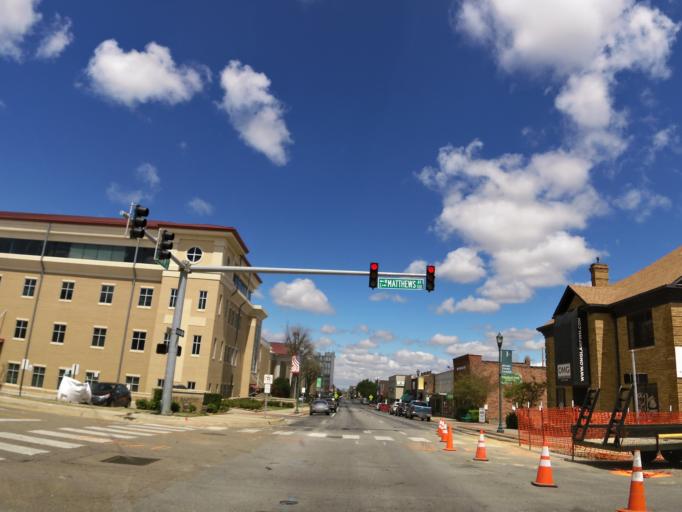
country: US
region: Arkansas
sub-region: Craighead County
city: Jonesboro
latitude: 35.8356
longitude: -90.7051
